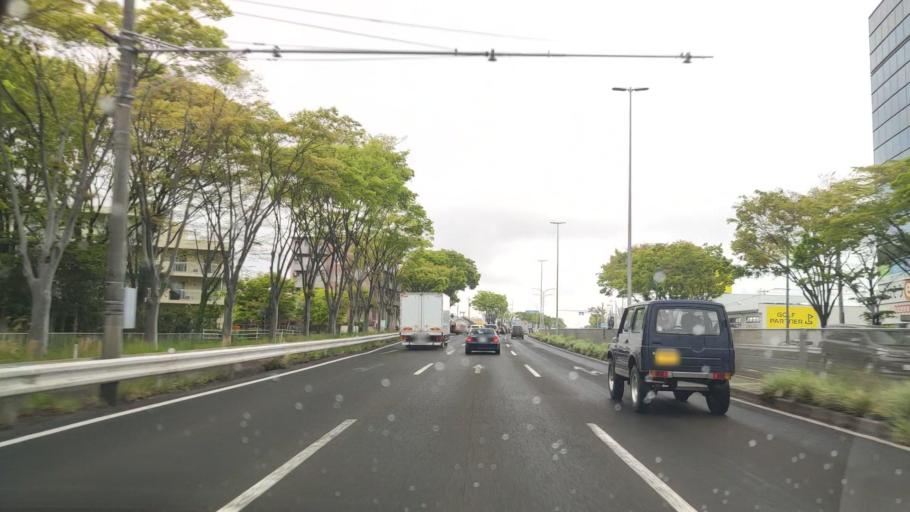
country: JP
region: Miyagi
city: Sendai
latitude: 38.2320
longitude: 140.9077
